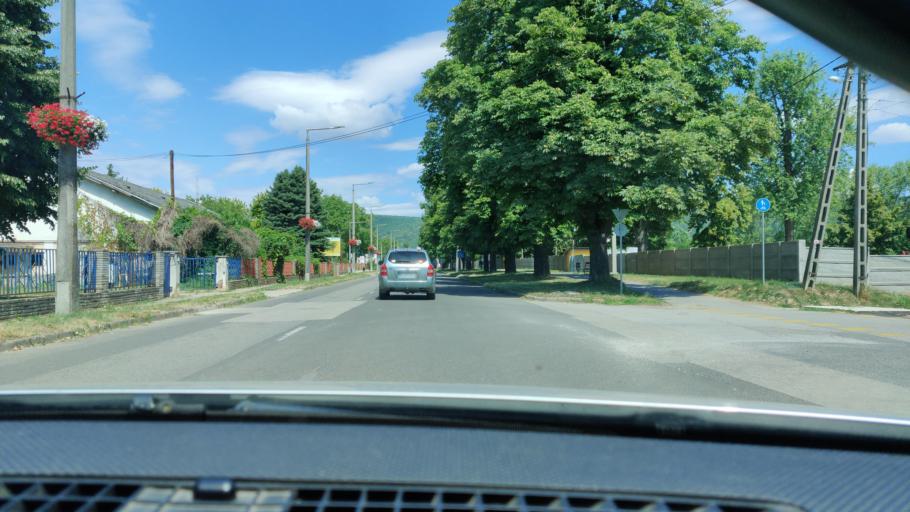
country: HU
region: Baranya
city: Siklos
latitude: 45.8608
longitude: 18.2887
